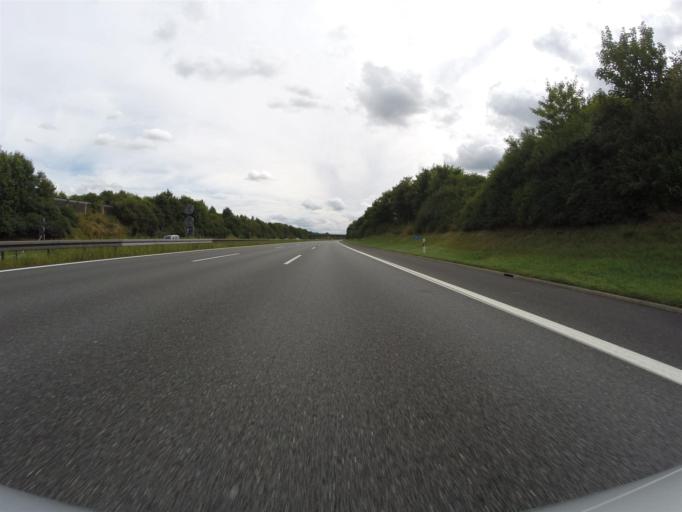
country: DE
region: Bavaria
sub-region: Upper Franconia
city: Bindlach
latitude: 49.9881
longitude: 11.6076
